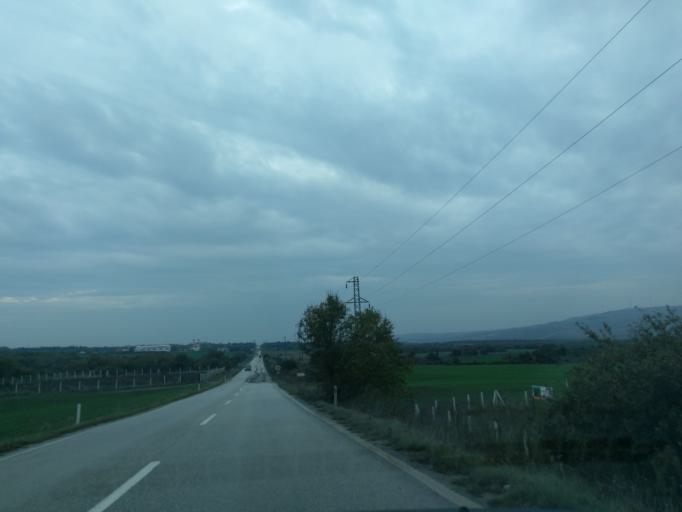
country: TR
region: Istanbul
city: Canta
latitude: 41.1515
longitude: 28.1068
